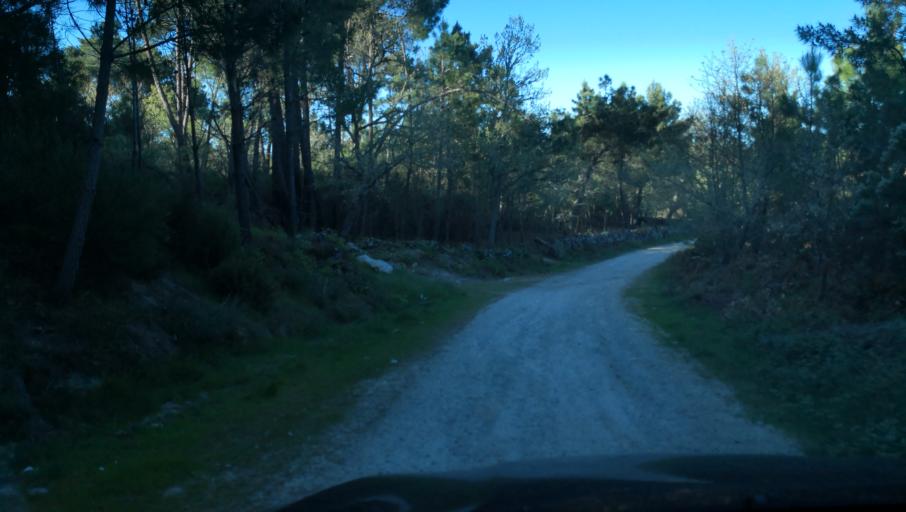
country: PT
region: Vila Real
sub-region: Vila Real
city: Vila Real
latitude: 41.3357
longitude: -7.6712
